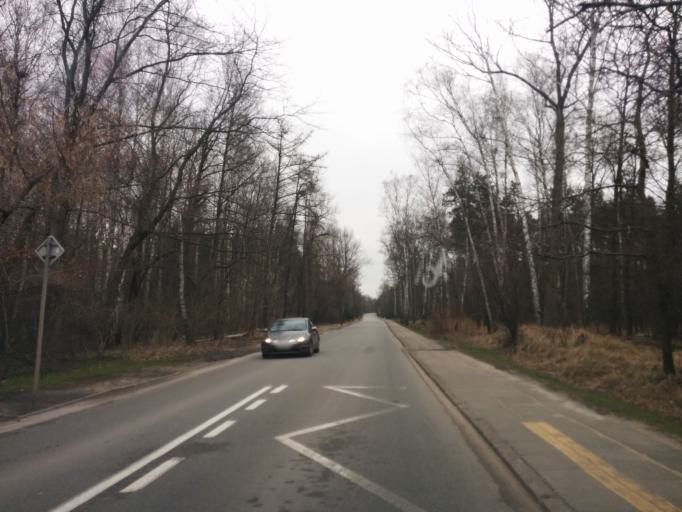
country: PL
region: Masovian Voivodeship
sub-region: Warszawa
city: Bialoleka
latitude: 52.3378
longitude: 20.9656
